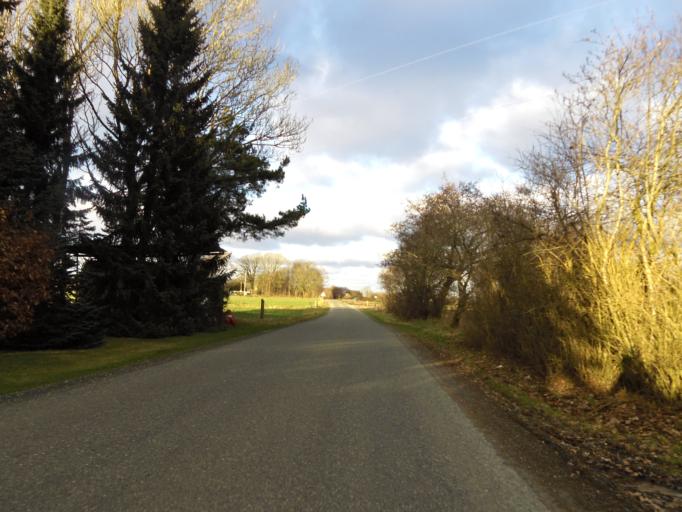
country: DK
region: South Denmark
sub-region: Esbjerg Kommune
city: Ribe
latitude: 55.2911
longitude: 8.8472
